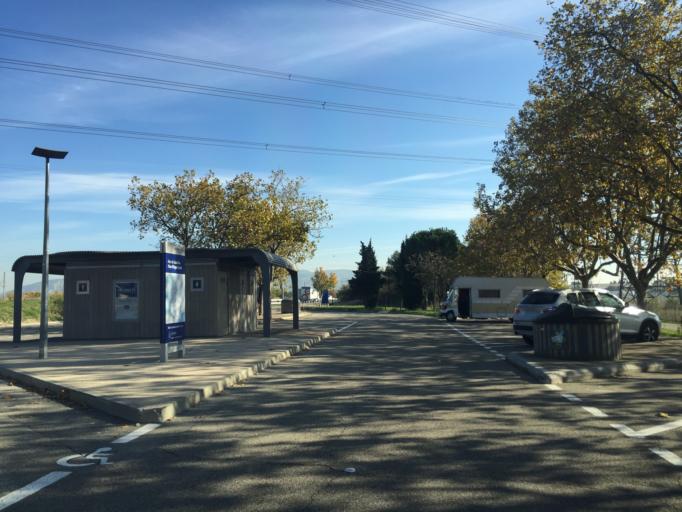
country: FR
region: Provence-Alpes-Cote d'Azur
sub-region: Departement du Vaucluse
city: Cavaillon
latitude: 43.8291
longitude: 5.0169
